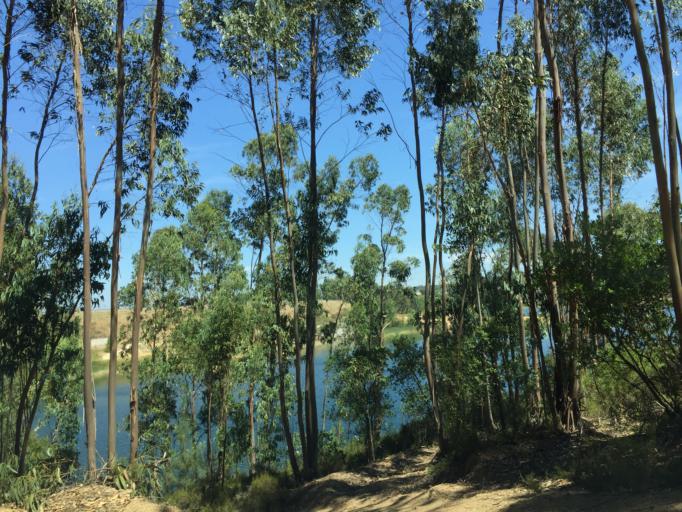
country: PT
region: Santarem
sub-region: Tomar
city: Tomar
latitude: 39.6137
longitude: -8.3603
